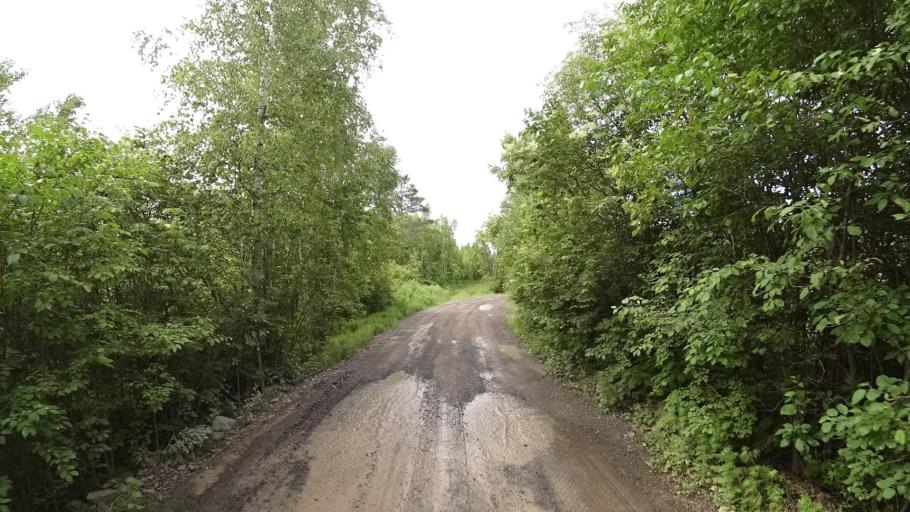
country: RU
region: Khabarovsk Krai
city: Amursk
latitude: 49.8995
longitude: 136.1502
